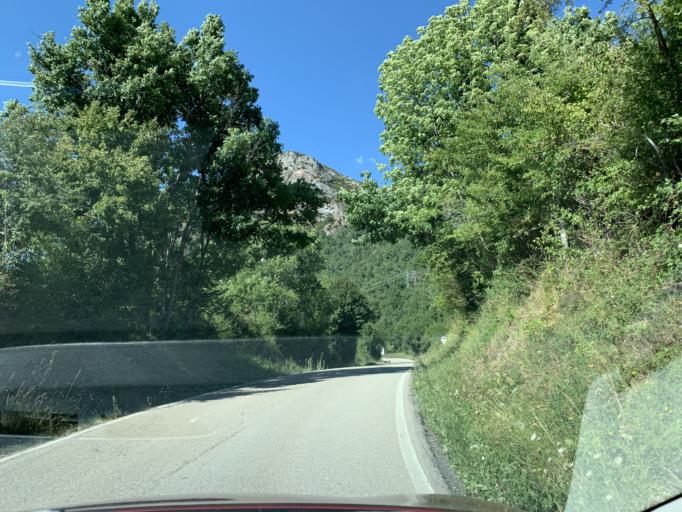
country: ES
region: Aragon
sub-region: Provincia de Huesca
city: Hoz de Jaca
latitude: 42.7254
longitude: -0.3023
